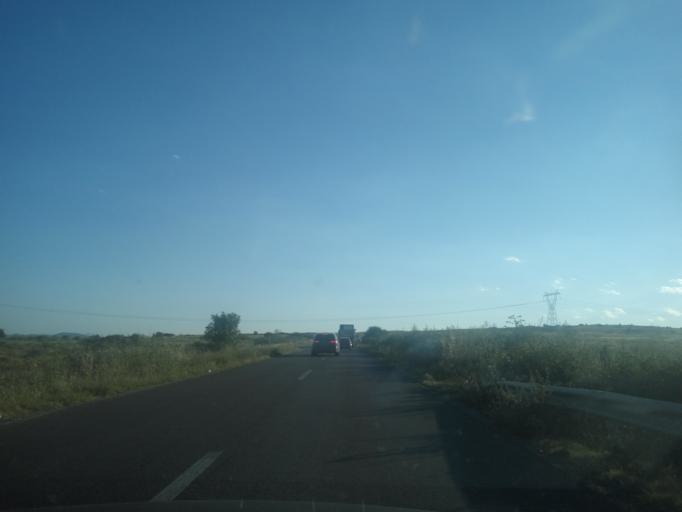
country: XK
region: Gjakova
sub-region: Komuna e Gjakoves
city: Gjakove
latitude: 42.4502
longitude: 20.4971
